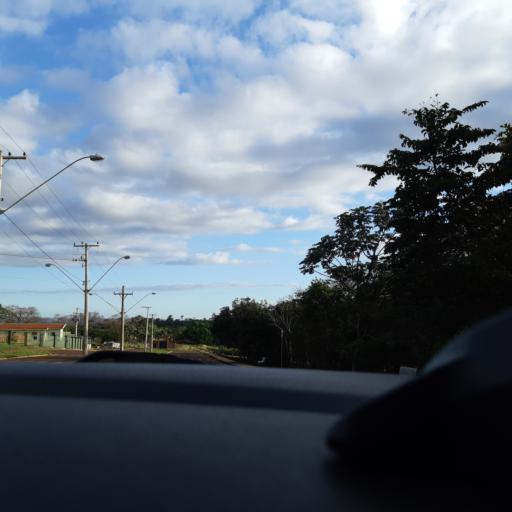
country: BR
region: Sao Paulo
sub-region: Ourinhos
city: Ourinhos
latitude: -23.0018
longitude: -49.8454
